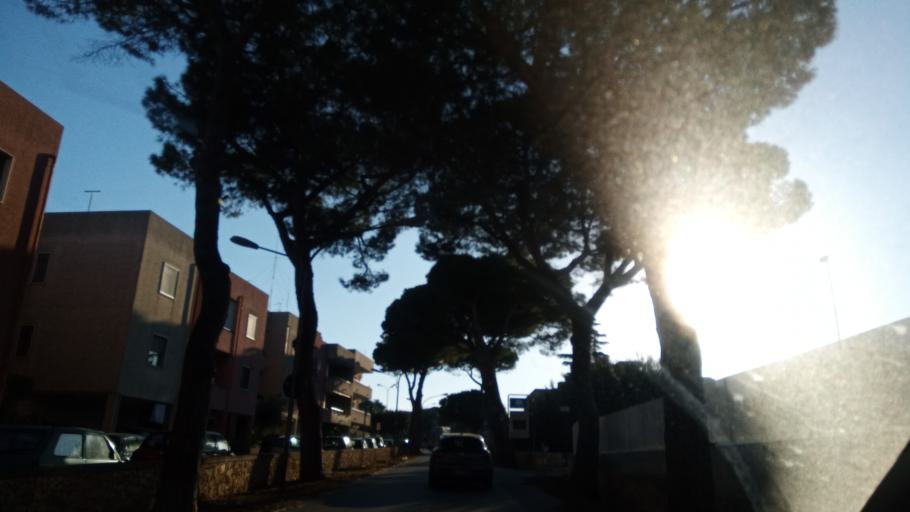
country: IT
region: Apulia
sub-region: Provincia di Bari
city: Polignano a Mare
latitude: 40.9912
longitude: 17.2163
